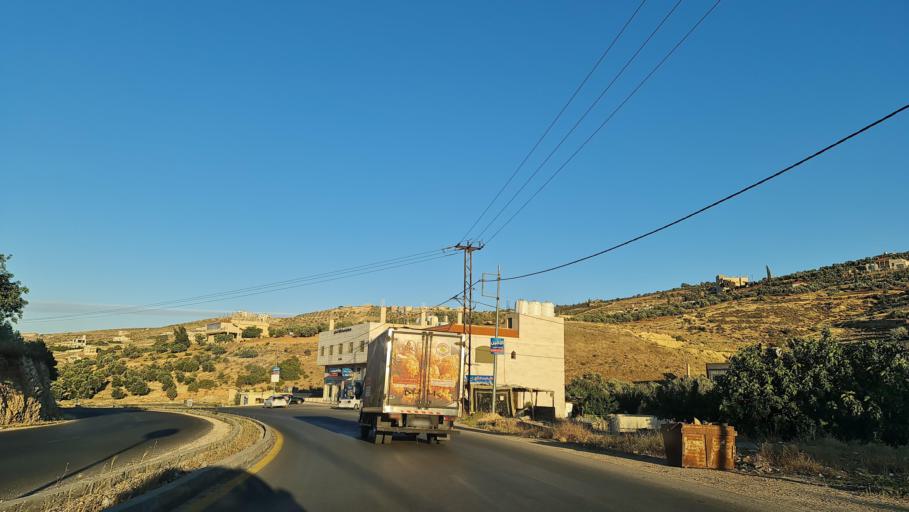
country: JO
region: Amman
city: Al Jubayhah
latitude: 32.0921
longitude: 35.9426
